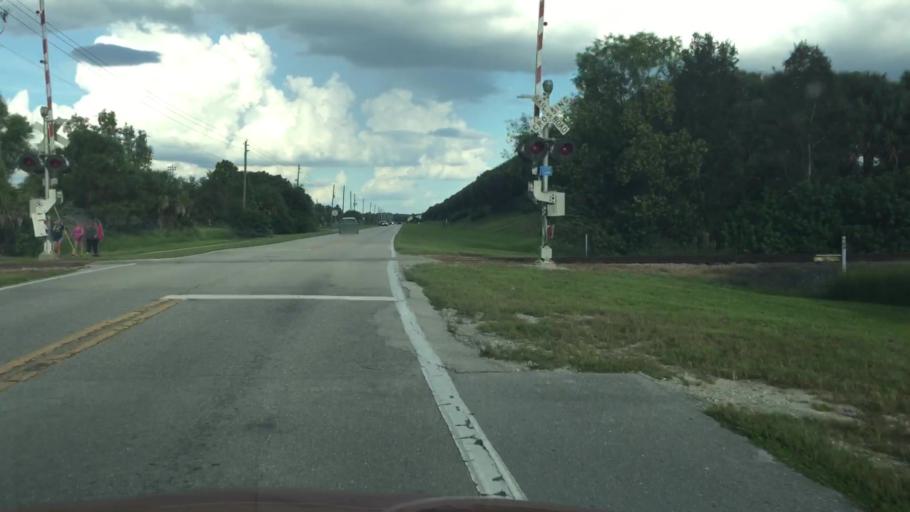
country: US
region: Florida
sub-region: Lee County
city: Estero
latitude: 26.4203
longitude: -81.8050
